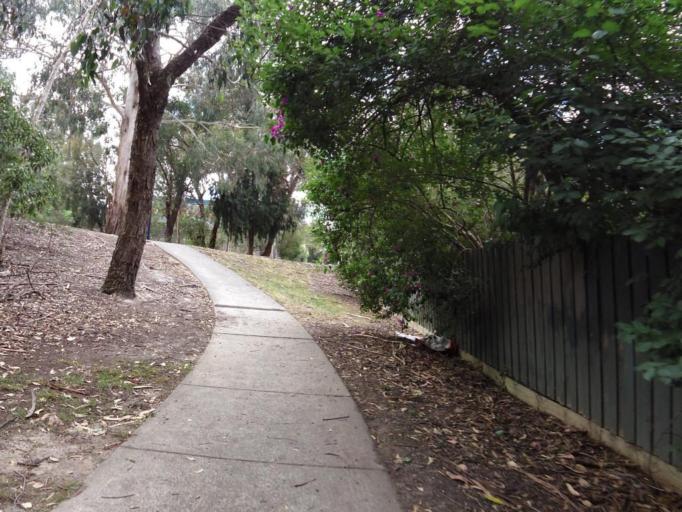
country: AU
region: Victoria
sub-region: Maroondah
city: Ringwood East
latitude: -37.8129
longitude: 145.2413
